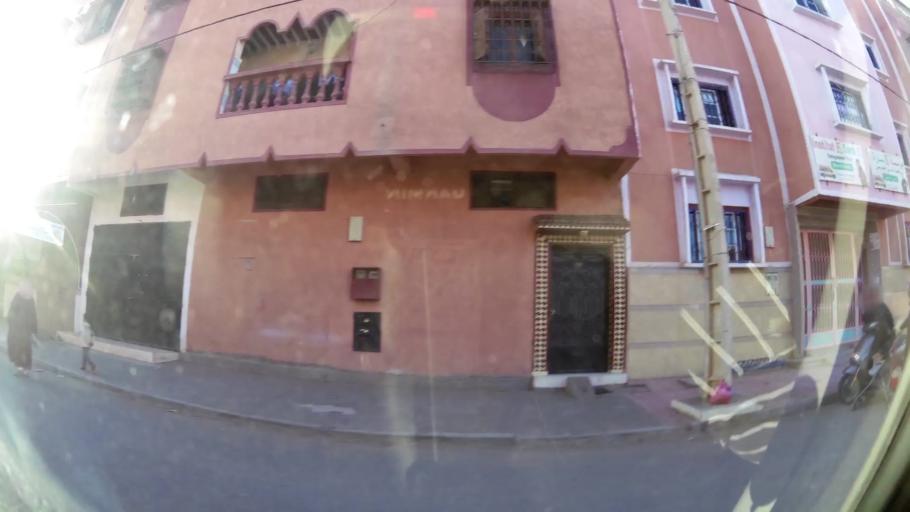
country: MA
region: Marrakech-Tensift-Al Haouz
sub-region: Marrakech
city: Marrakesh
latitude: 31.6197
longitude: -8.0611
